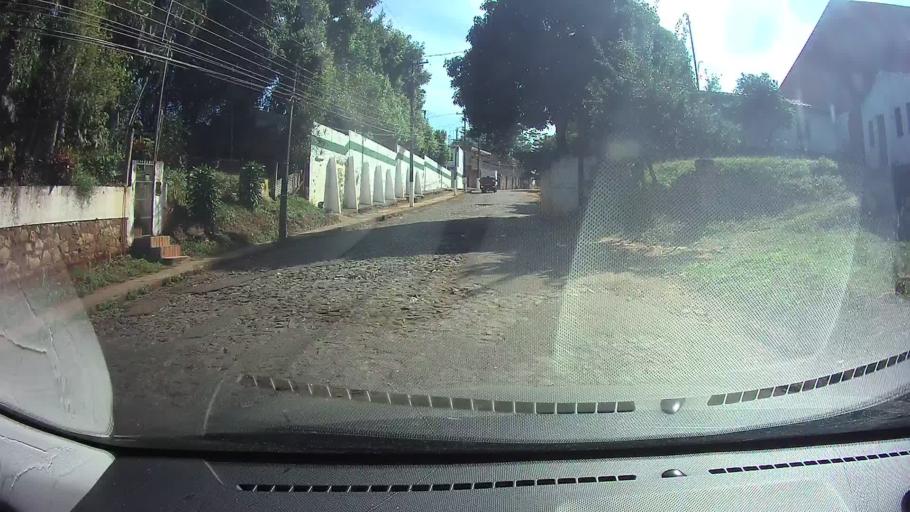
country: PY
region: Central
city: Villa Elisa
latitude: -25.3605
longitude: -57.5694
